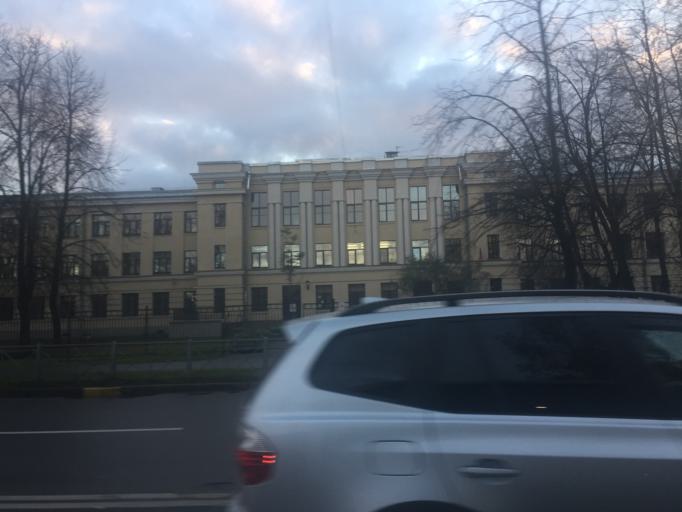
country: RU
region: St.-Petersburg
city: Obukhovo
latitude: 59.8791
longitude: 30.4402
